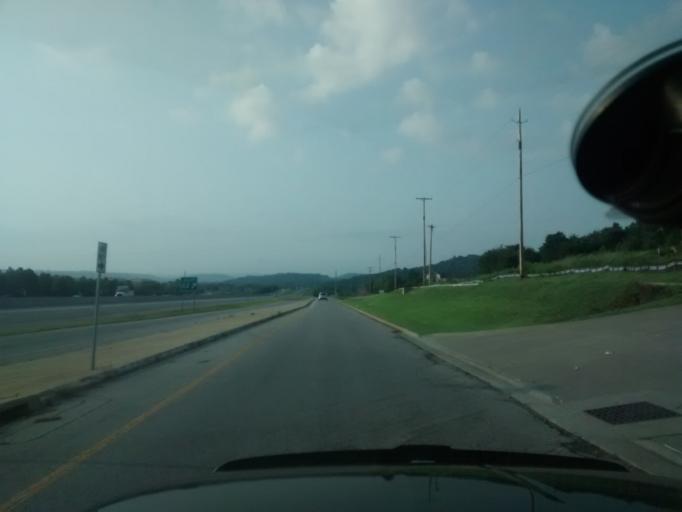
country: US
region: Arkansas
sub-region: Washington County
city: Fayetteville
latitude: 36.0612
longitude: -94.1989
